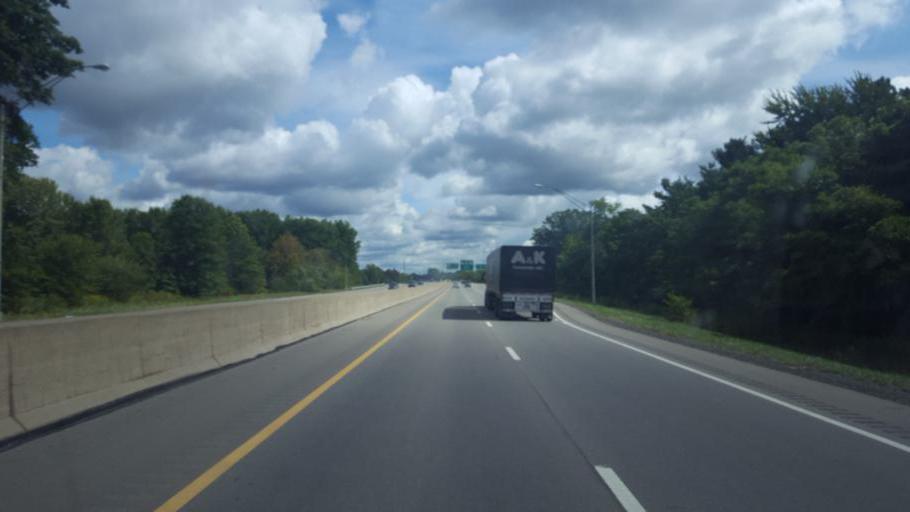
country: US
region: Ohio
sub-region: Lorain County
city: Elyria
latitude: 41.3273
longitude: -82.0815
